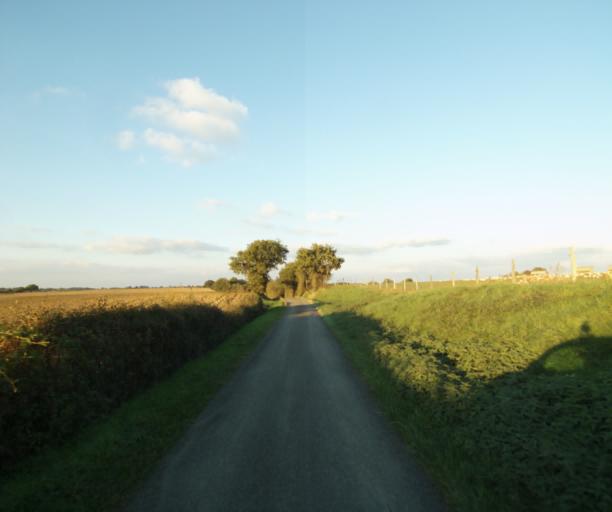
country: FR
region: Midi-Pyrenees
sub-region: Departement du Gers
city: Vic-Fezensac
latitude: 43.7437
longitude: 0.1868
